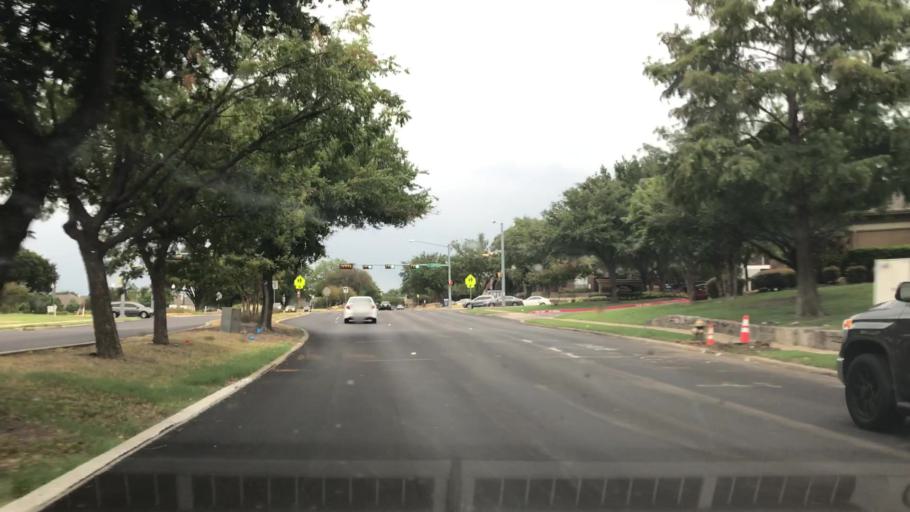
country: US
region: Texas
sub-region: Dallas County
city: Coppell
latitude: 32.9472
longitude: -96.9553
